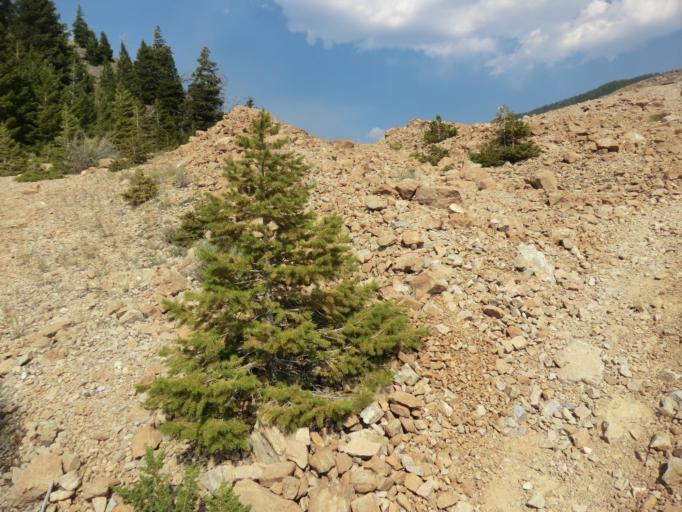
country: US
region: Montana
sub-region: Gallatin County
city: West Yellowstone
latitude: 44.8296
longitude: -111.4313
